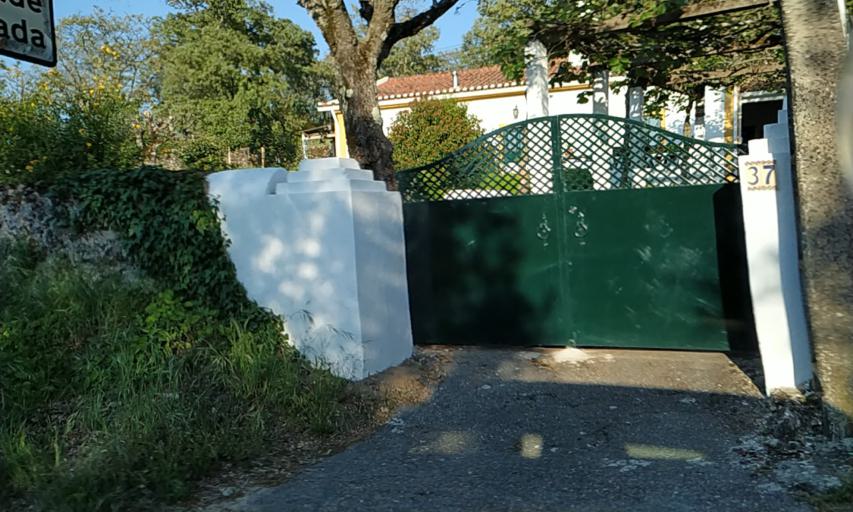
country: PT
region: Portalegre
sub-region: Marvao
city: Marvao
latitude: 39.3568
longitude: -7.4067
